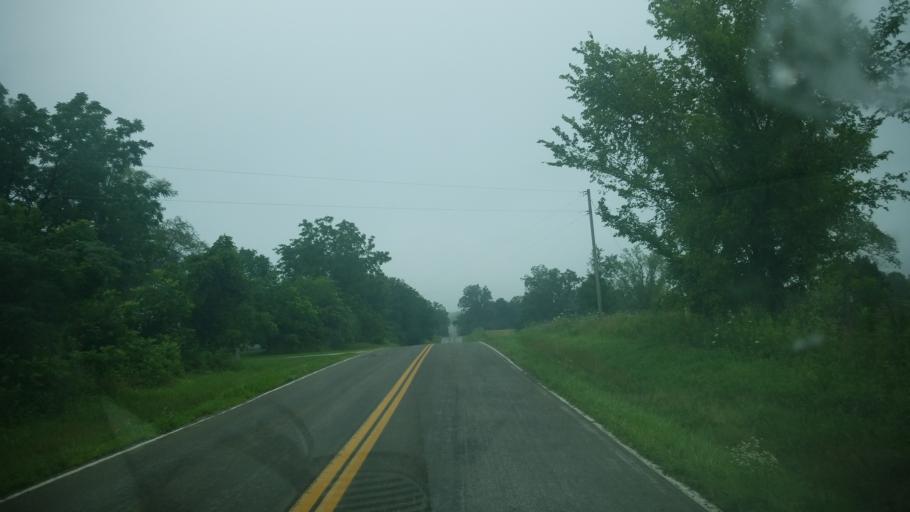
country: US
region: Missouri
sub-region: Audrain County
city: Vandalia
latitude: 39.3080
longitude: -91.3451
